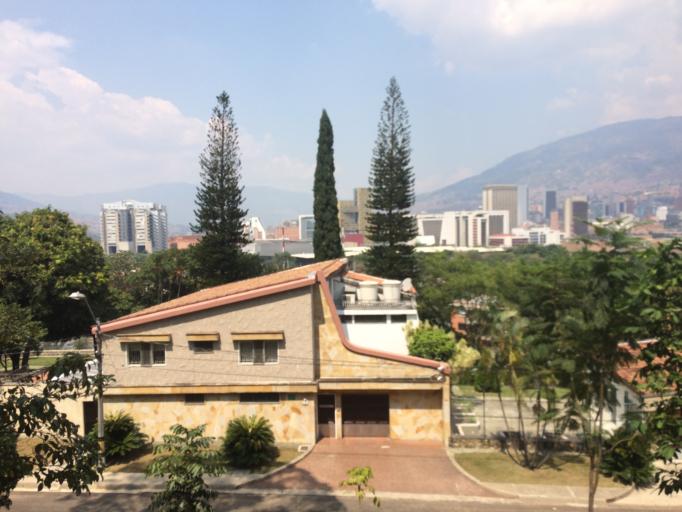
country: CO
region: Antioquia
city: Medellin
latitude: 6.2375
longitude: -75.5786
